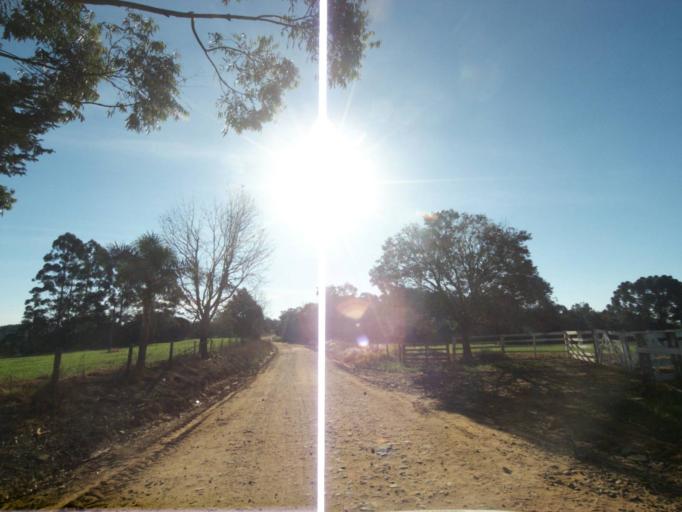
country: BR
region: Parana
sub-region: Telemaco Borba
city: Telemaco Borba
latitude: -24.5233
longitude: -50.6395
